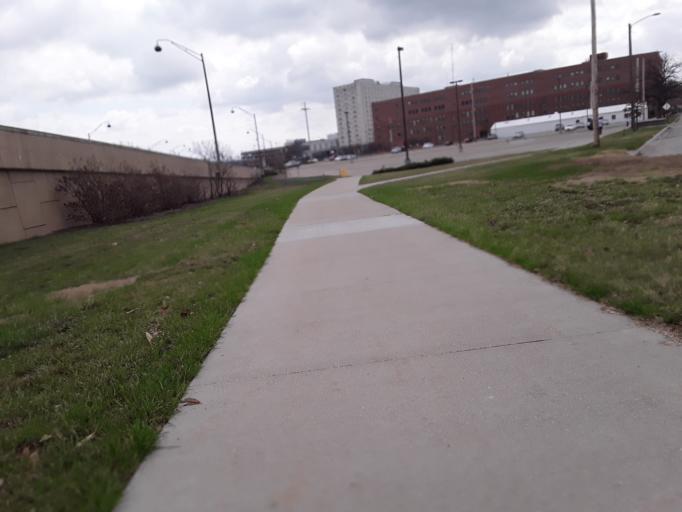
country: US
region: Nebraska
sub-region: Lancaster County
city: Lincoln
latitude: 40.8254
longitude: -96.6981
